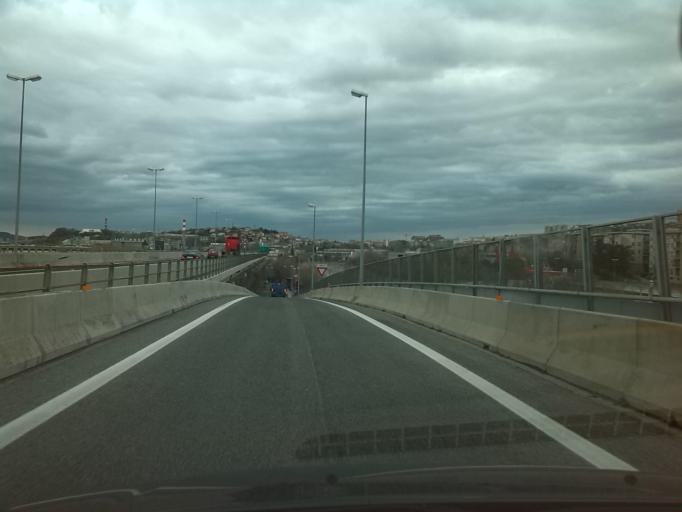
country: IT
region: Friuli Venezia Giulia
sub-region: Provincia di Trieste
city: Domio
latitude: 45.6167
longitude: 13.8180
